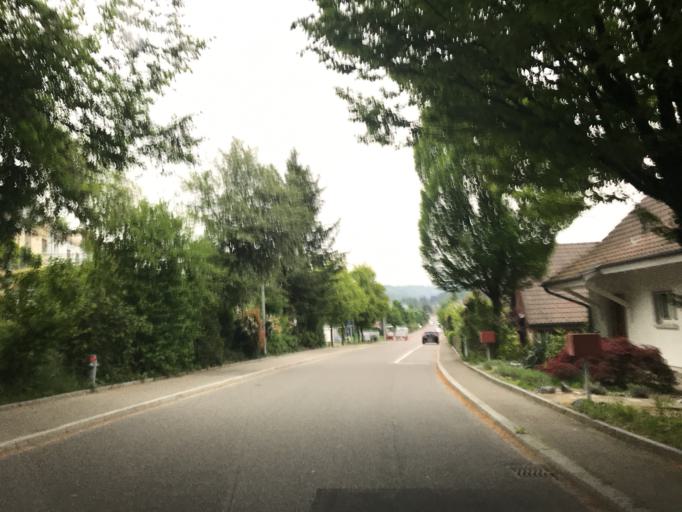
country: CH
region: Zurich
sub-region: Bezirk Winterthur
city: Toess (Kreis 4) / Vorder-Daettnau
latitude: 47.4830
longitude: 8.6951
